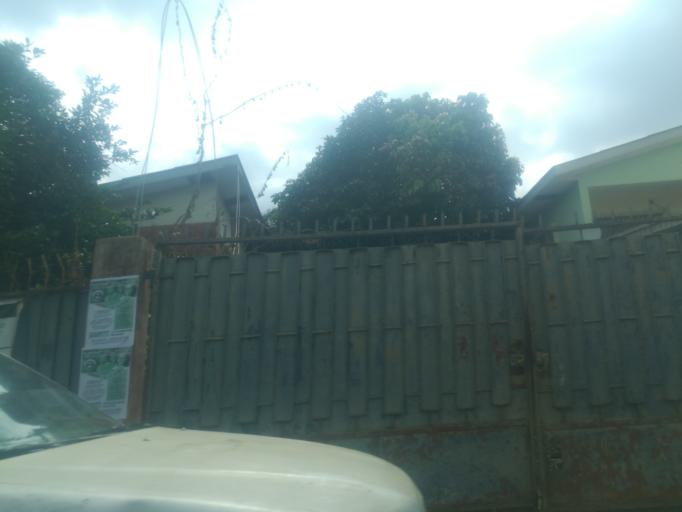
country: NG
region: Oyo
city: Ibadan
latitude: 7.4061
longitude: 3.9294
